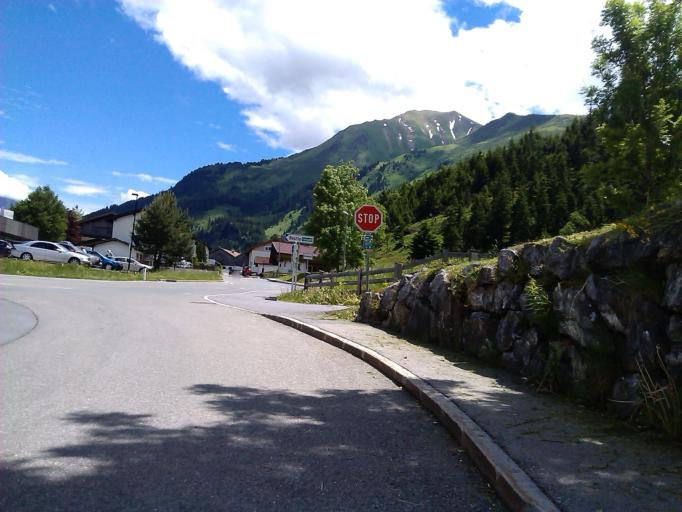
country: AT
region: Tyrol
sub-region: Politischer Bezirk Reutte
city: Bichlbach
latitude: 47.4227
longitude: 10.7827
